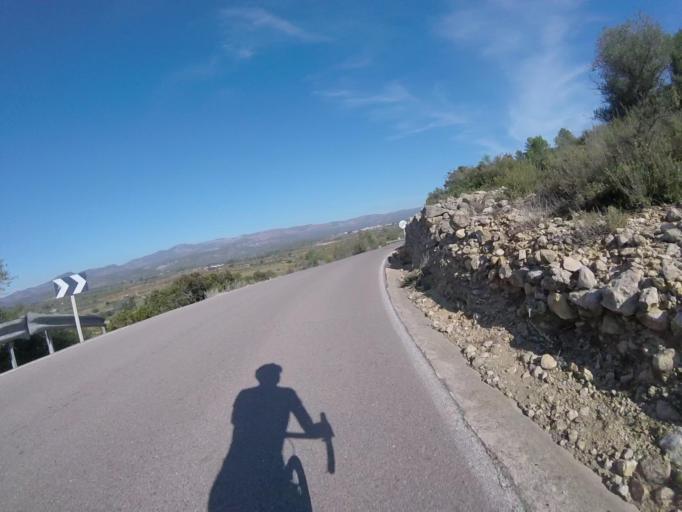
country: ES
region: Valencia
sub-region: Provincia de Castello
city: Benlloch
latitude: 40.2465
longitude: 0.0769
